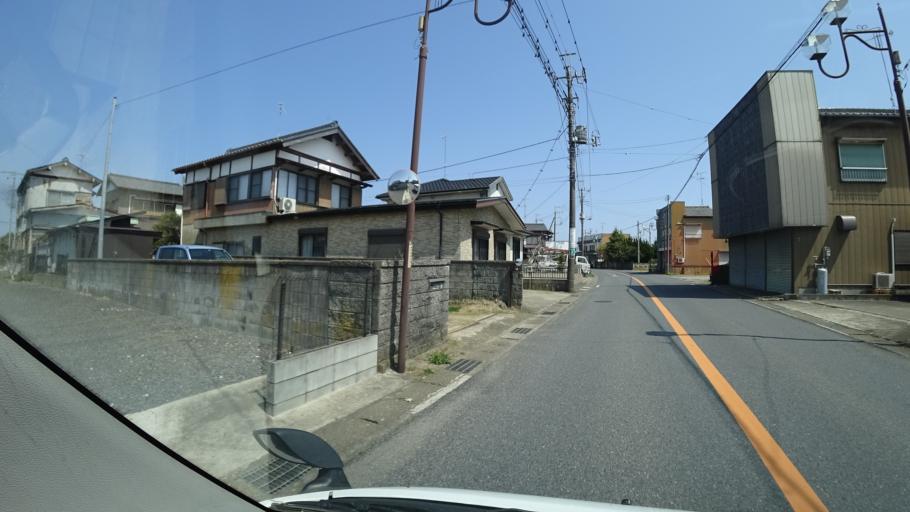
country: JP
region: Chiba
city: Naruto
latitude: 35.6572
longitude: 140.4774
